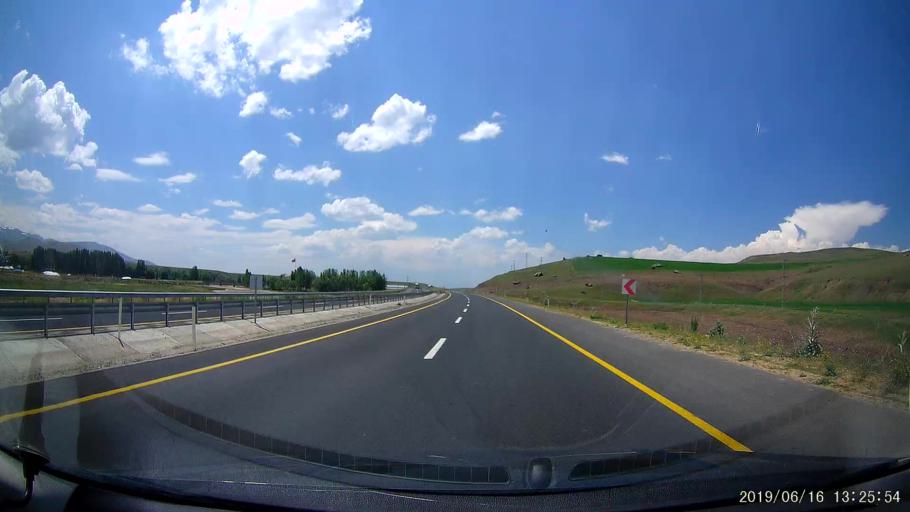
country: TR
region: Agri
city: Taslicay
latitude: 39.6563
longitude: 43.3416
